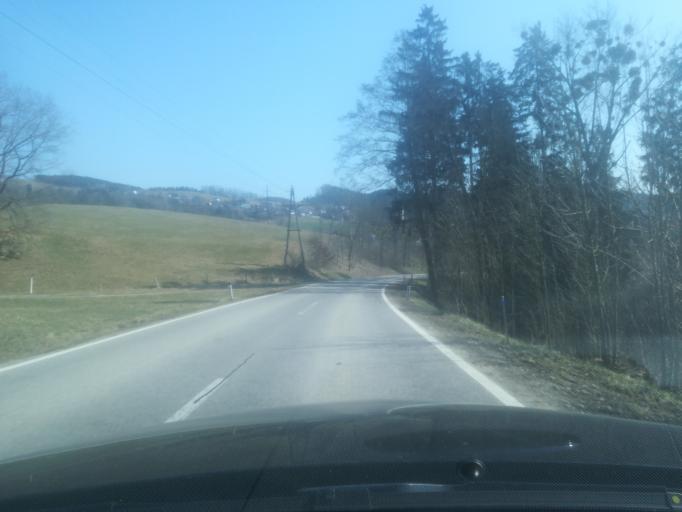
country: AT
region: Upper Austria
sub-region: Politischer Bezirk Freistadt
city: Freistadt
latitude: 48.4470
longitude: 14.5281
